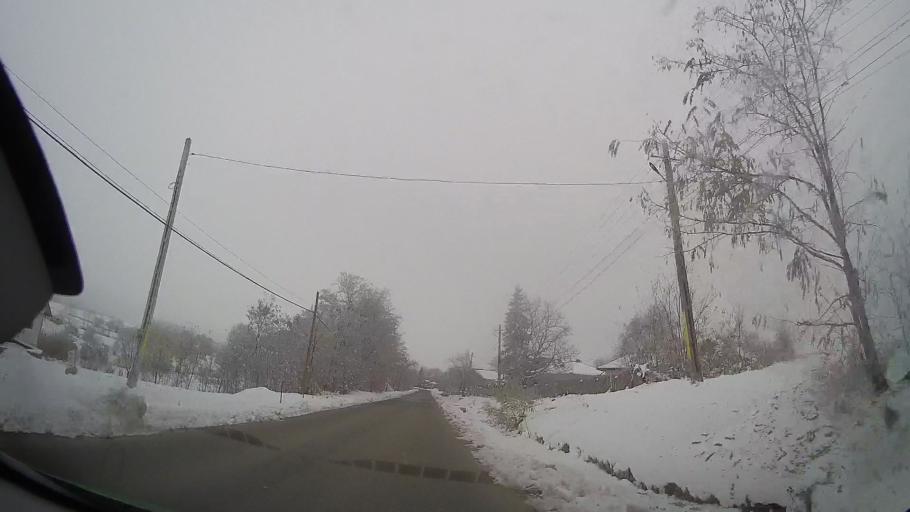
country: RO
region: Neamt
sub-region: Comuna Icusesti
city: Balusesti
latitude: 46.8595
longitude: 27.0211
